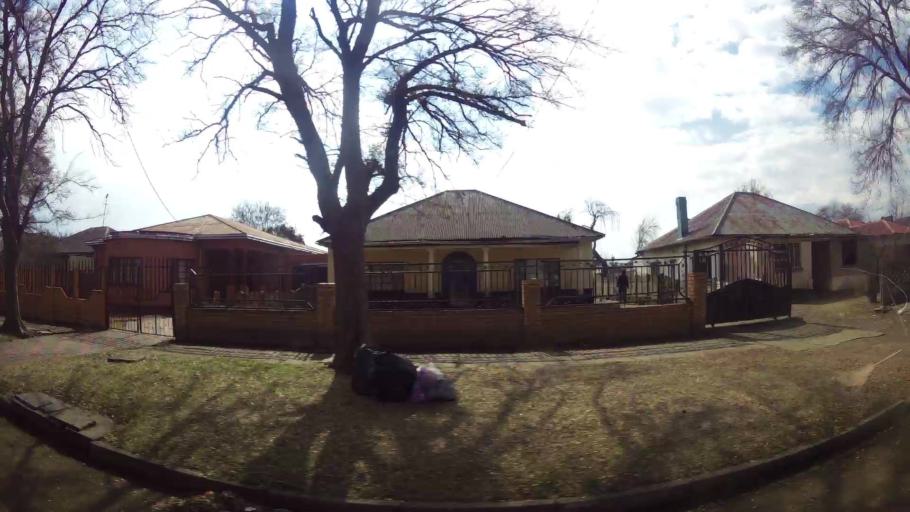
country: ZA
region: Gauteng
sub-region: Sedibeng District Municipality
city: Vereeniging
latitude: -26.6679
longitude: 27.9233
